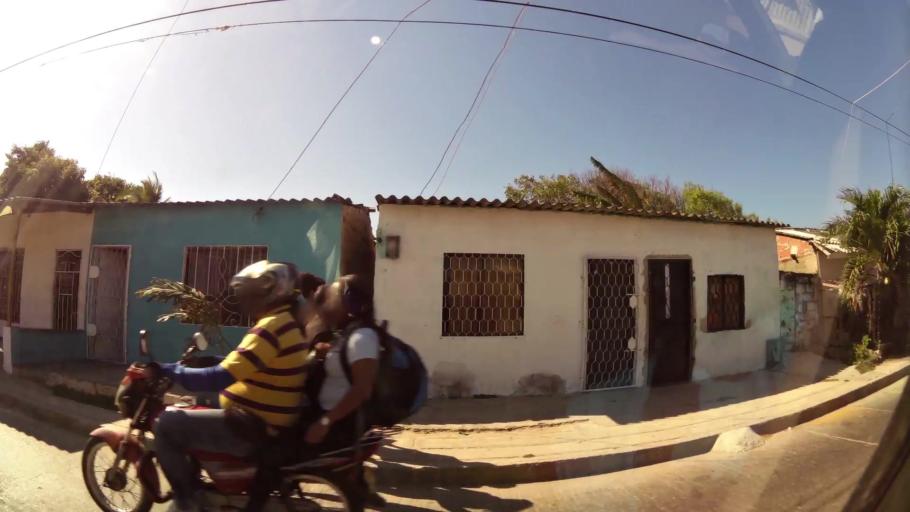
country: CO
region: Atlantico
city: Barranquilla
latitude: 10.9340
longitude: -74.8113
